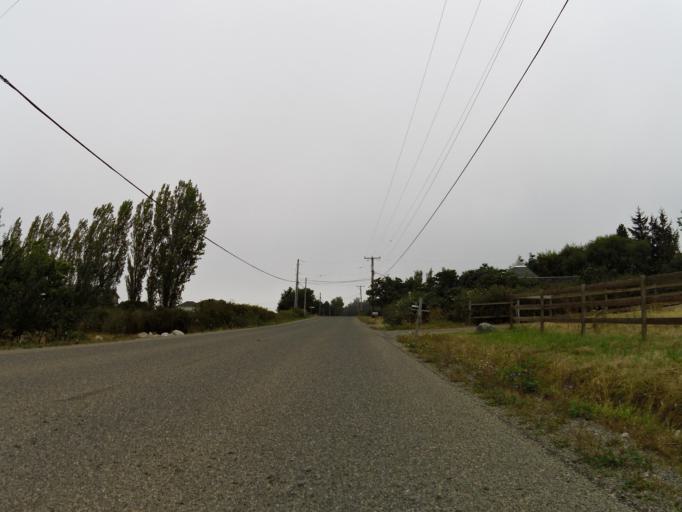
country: US
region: Washington
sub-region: Island County
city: Ault Field
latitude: 48.3040
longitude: -122.7129
